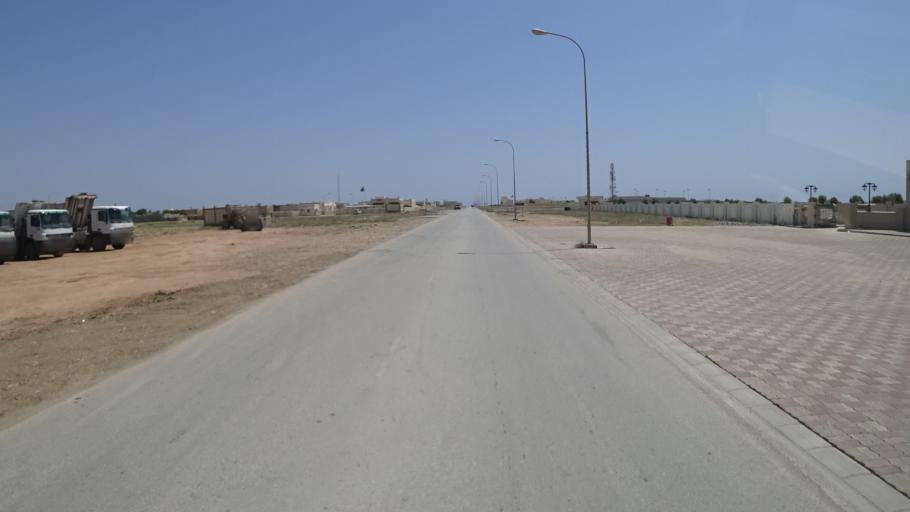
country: OM
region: Zufar
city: Salalah
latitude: 16.9876
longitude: 54.6969
